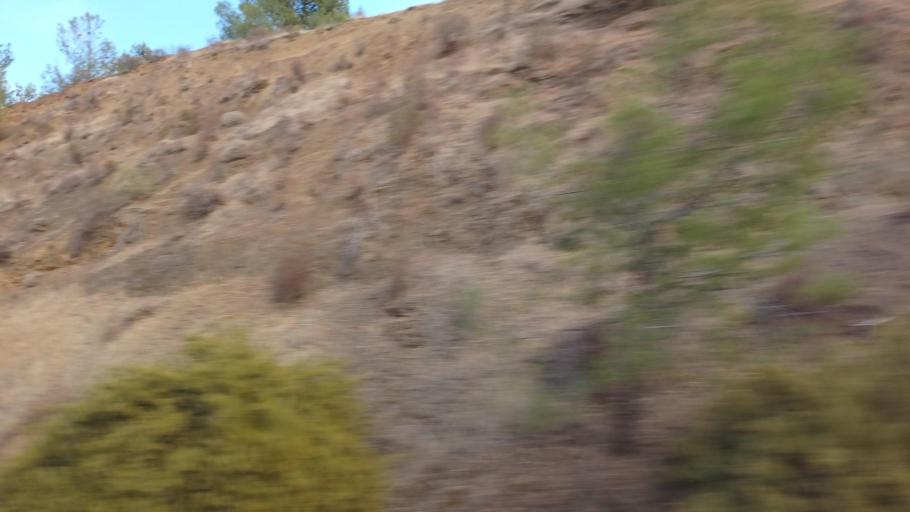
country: CY
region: Lefkosia
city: Kakopetria
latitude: 35.0267
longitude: 32.9007
